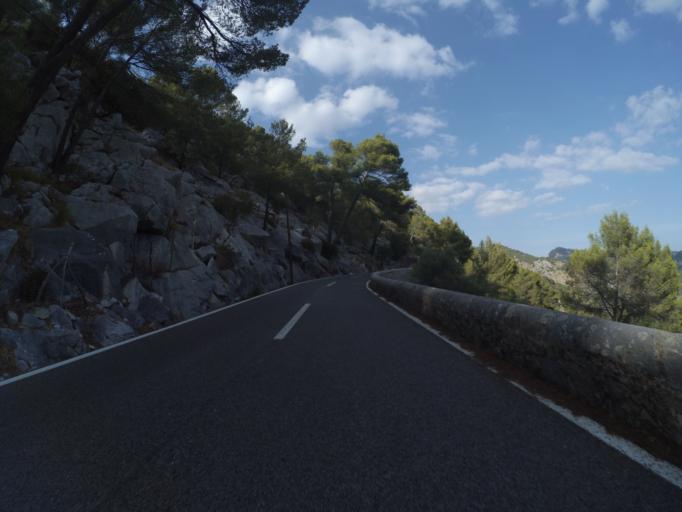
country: ES
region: Balearic Islands
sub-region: Illes Balears
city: Escorca
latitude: 39.7938
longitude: 2.8949
